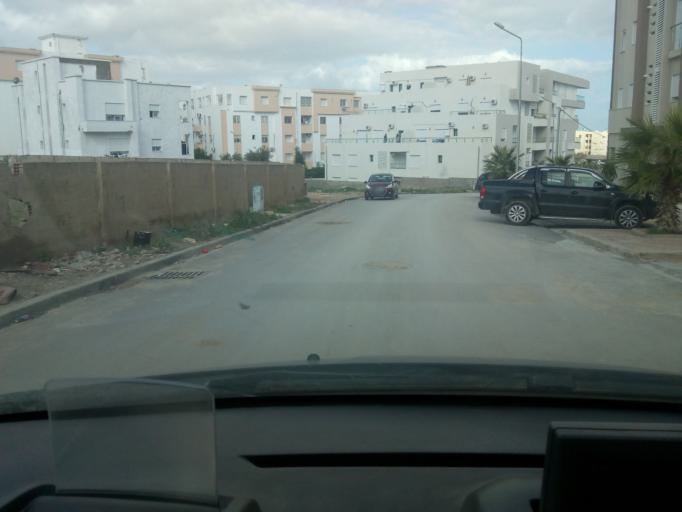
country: TN
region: Ariana
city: Ariana
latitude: 36.8766
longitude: 10.1772
